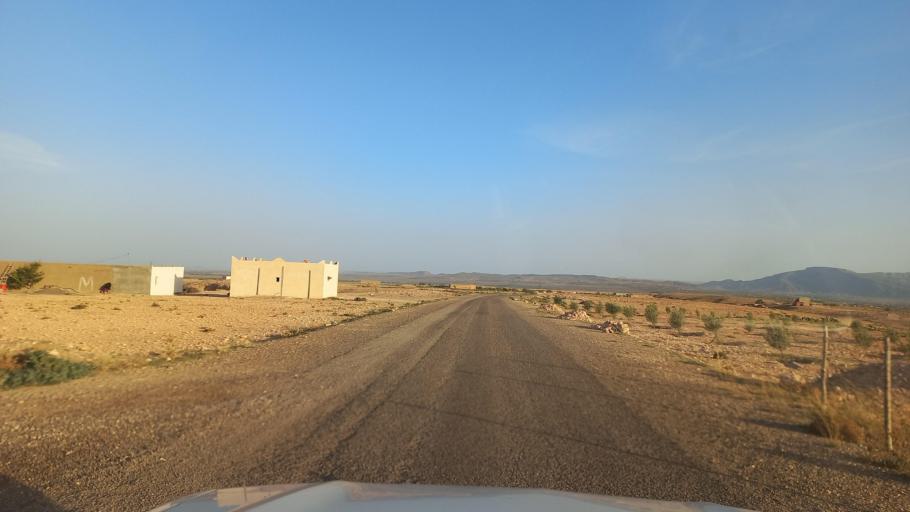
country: TN
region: Al Qasrayn
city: Kasserine
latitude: 35.2753
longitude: 8.9125
